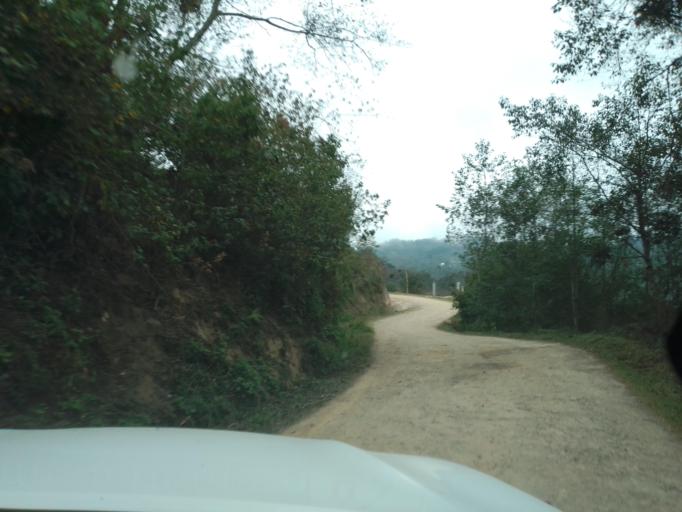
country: MX
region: Chiapas
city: Motozintla de Mendoza
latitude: 15.2190
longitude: -92.2297
